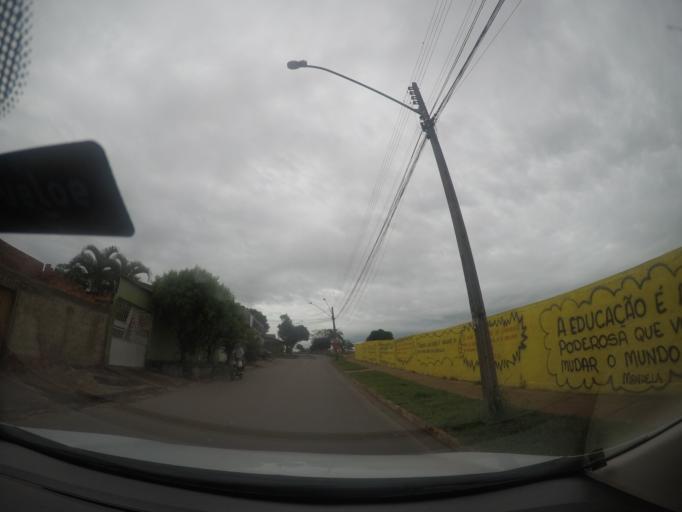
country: BR
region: Goias
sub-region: Goiania
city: Goiania
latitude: -16.6101
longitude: -49.3120
